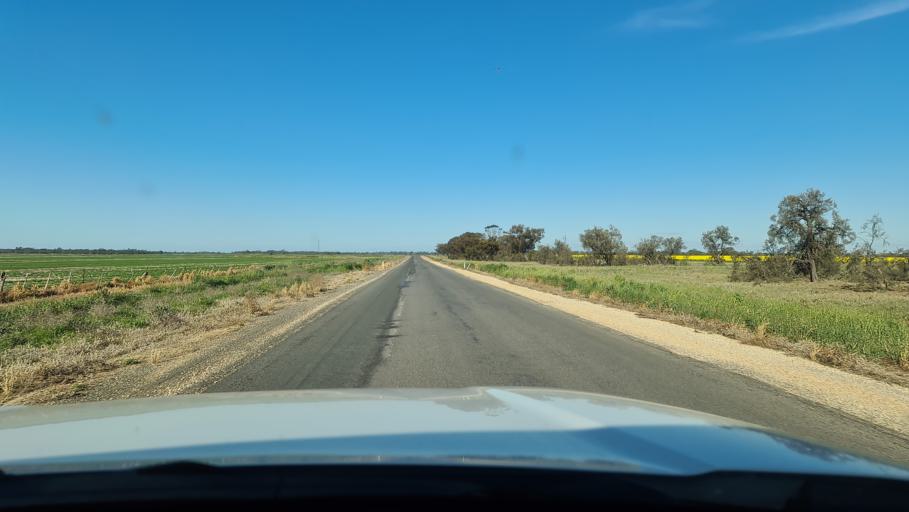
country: AU
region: Victoria
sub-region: Horsham
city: Horsham
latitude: -36.4492
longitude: 142.5625
